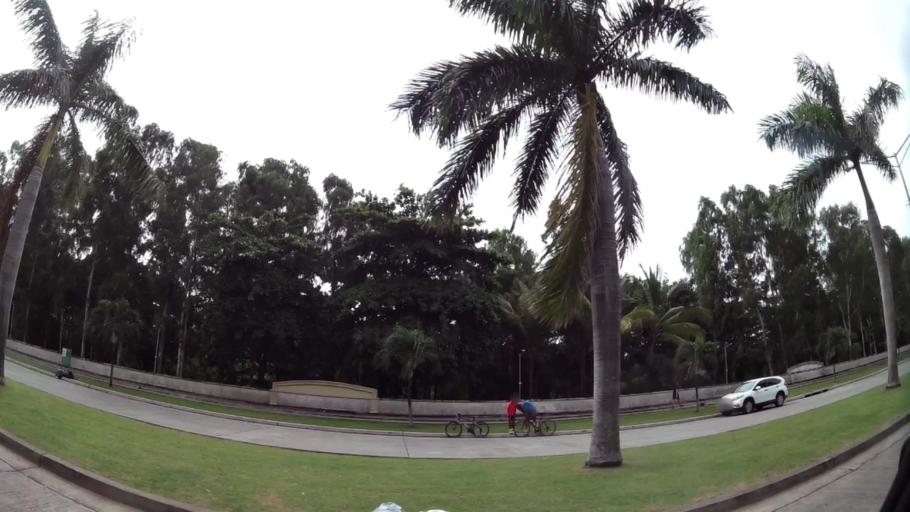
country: PA
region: Panama
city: San Miguelito
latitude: 9.0079
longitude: -79.4774
